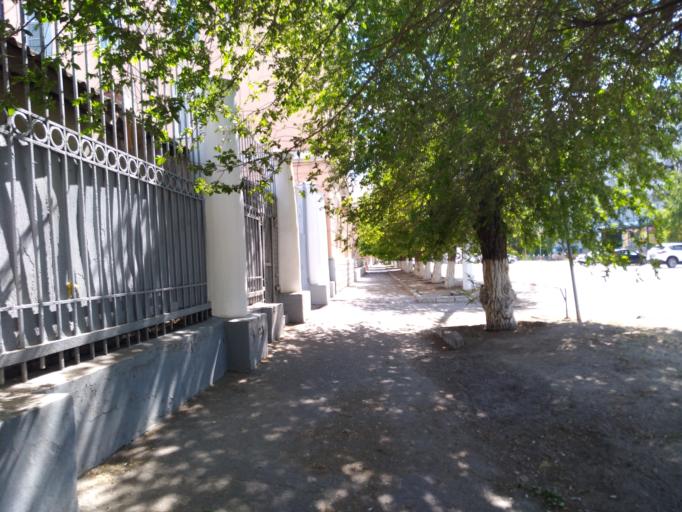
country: RU
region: Volgograd
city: Volgograd
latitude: 48.7164
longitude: 44.5251
